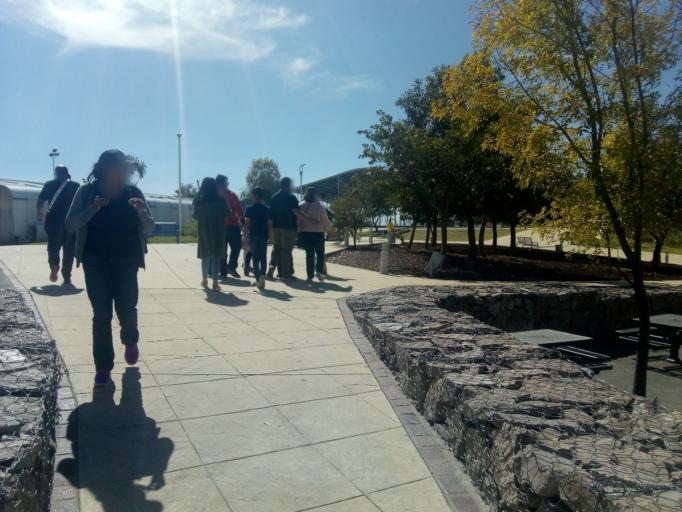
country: MX
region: Guanajuato
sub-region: Silao de la Victoria
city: Aguas Buenas
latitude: 20.9563
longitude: -101.3609
